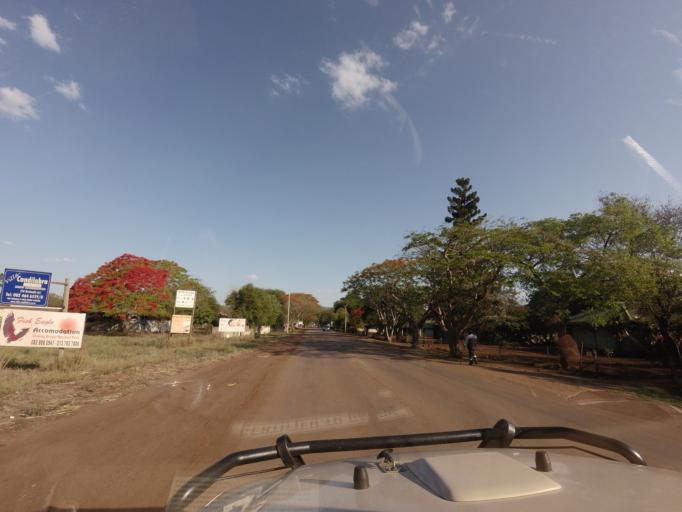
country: ZA
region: Mpumalanga
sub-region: Ehlanzeni District
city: Komatipoort
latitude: -25.4296
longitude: 31.9495
